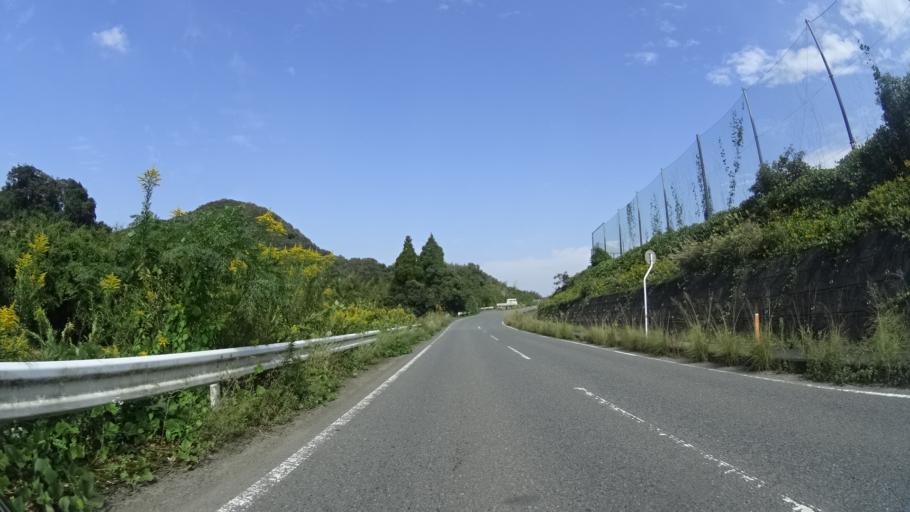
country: JP
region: Kumamoto
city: Uto
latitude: 32.6738
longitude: 130.7210
